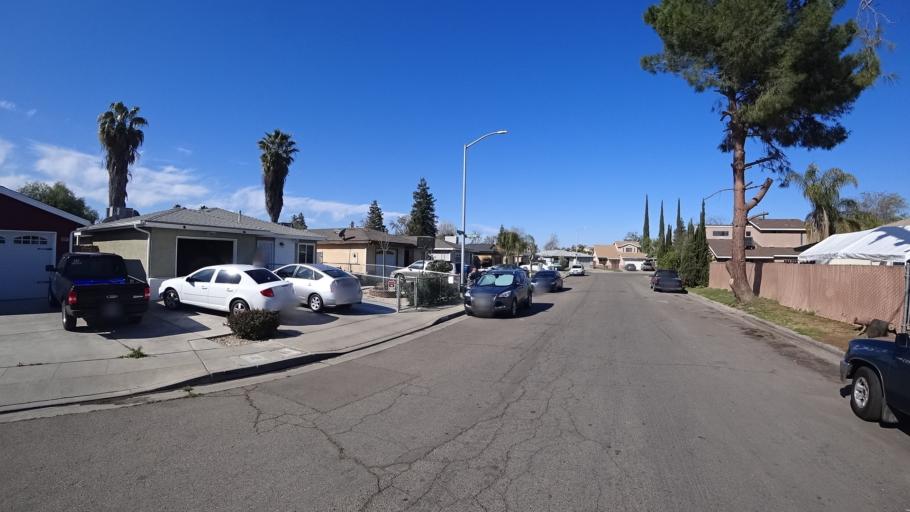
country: US
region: California
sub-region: Fresno County
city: West Park
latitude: 36.7994
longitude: -119.8833
